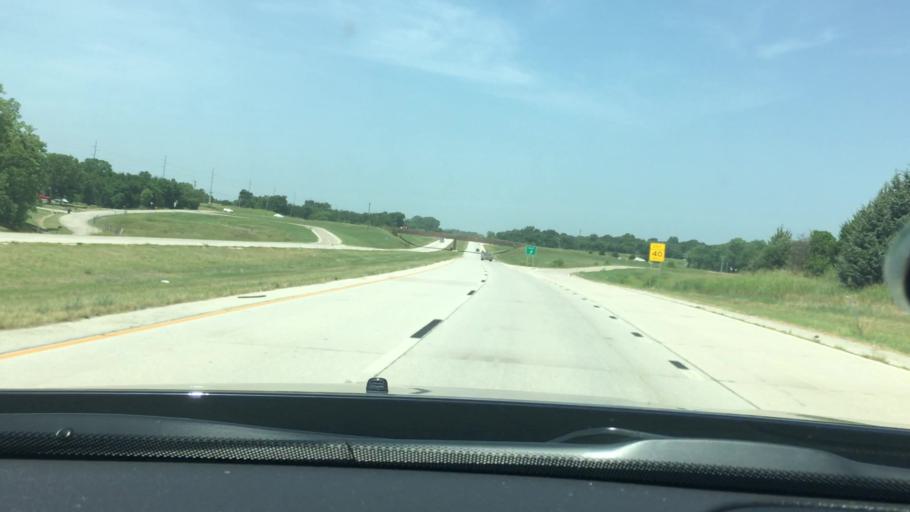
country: US
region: Oklahoma
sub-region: Pontotoc County
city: Ada
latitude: 34.7524
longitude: -96.6652
